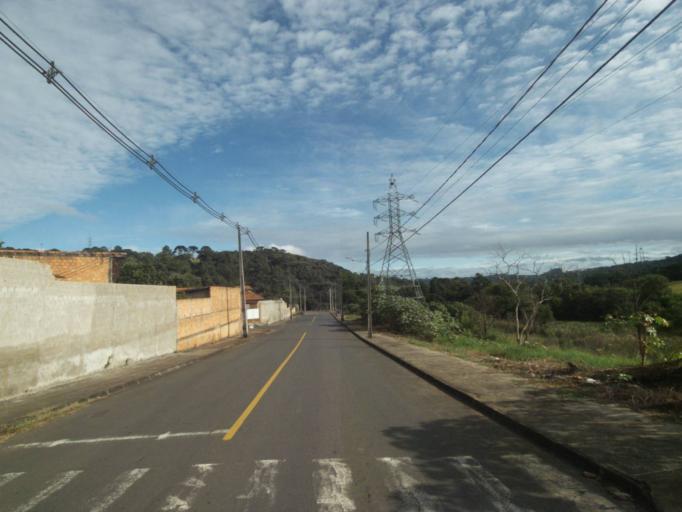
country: BR
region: Parana
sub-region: Telemaco Borba
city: Telemaco Borba
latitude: -24.3437
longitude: -50.6059
